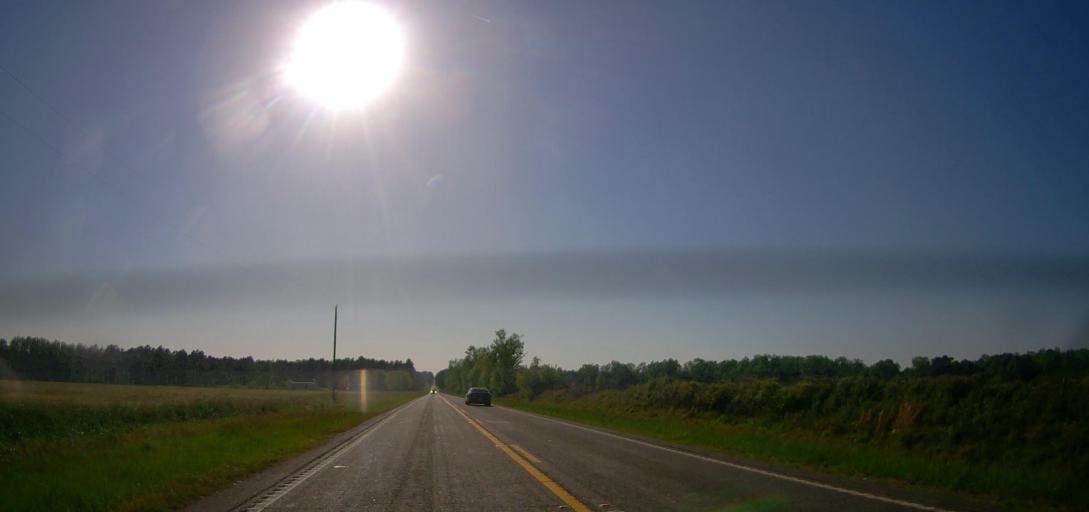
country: US
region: Georgia
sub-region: Ben Hill County
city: Fitzgerald
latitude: 31.7189
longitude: -83.3521
